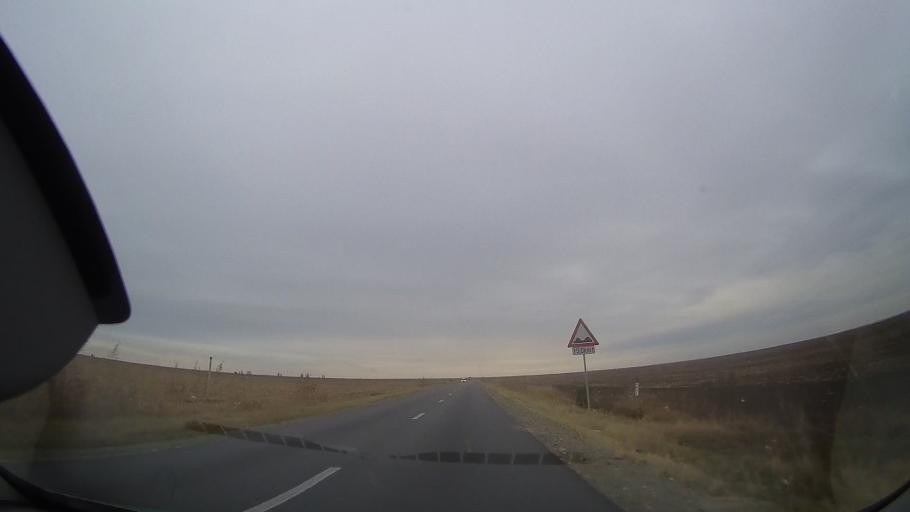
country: RO
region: Ialomita
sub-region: Oras Amara
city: Amara
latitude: 44.6467
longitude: 27.3005
